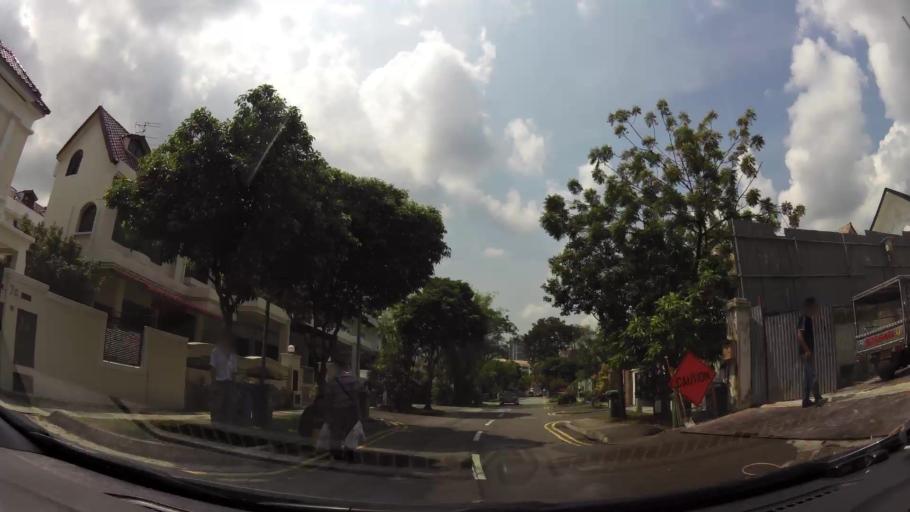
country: SG
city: Singapore
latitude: 1.3231
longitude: 103.8101
